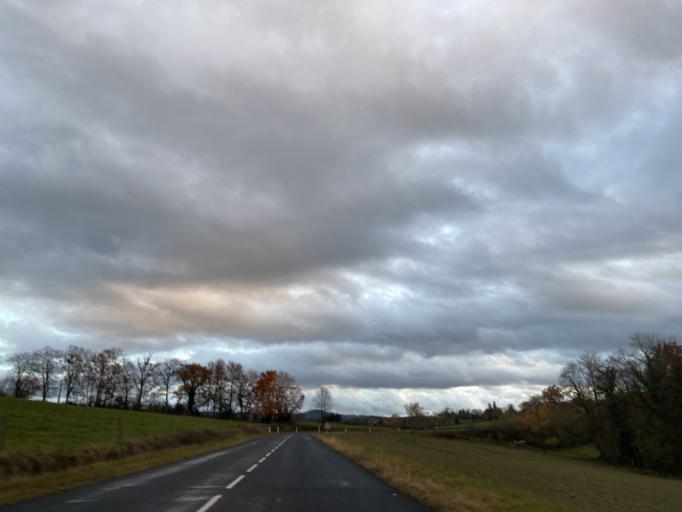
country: FR
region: Auvergne
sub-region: Departement du Puy-de-Dome
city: Cunlhat
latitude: 45.6812
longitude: 3.5789
